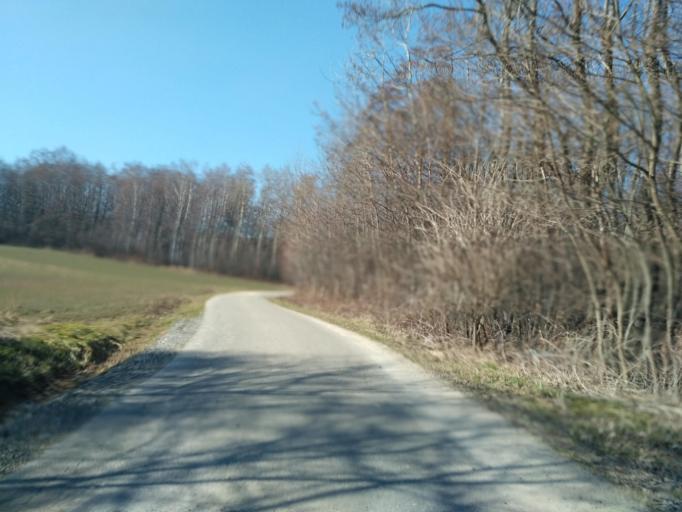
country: PL
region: Subcarpathian Voivodeship
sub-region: Powiat rzeszowski
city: Zglobien
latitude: 49.9875
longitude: 21.8412
